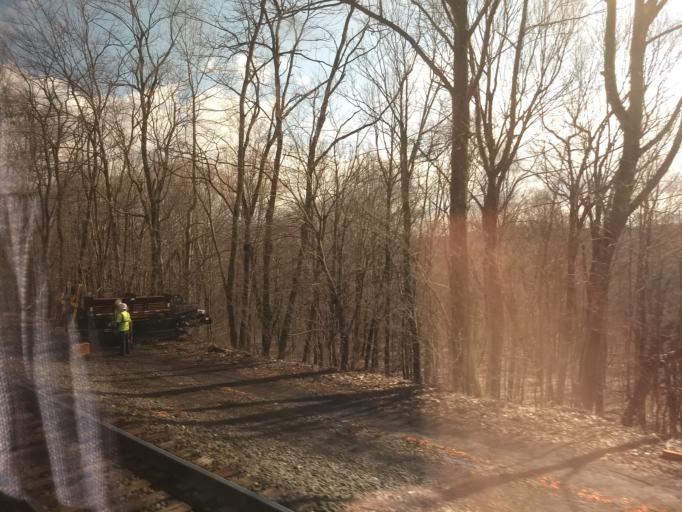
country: US
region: Pennsylvania
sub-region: Blair County
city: Duncansville
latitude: 40.4806
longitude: -78.4772
